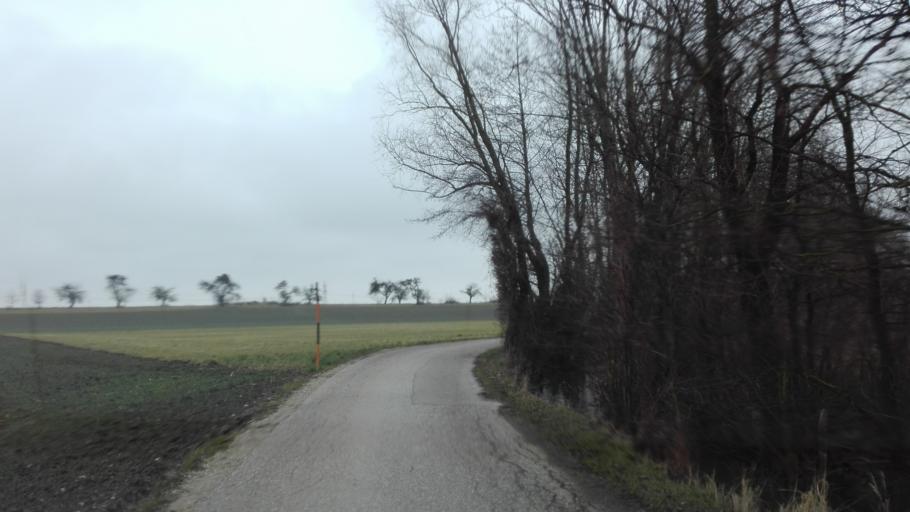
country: AT
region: Upper Austria
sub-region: Wels-Land
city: Marchtrenk
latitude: 48.2112
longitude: 14.1400
